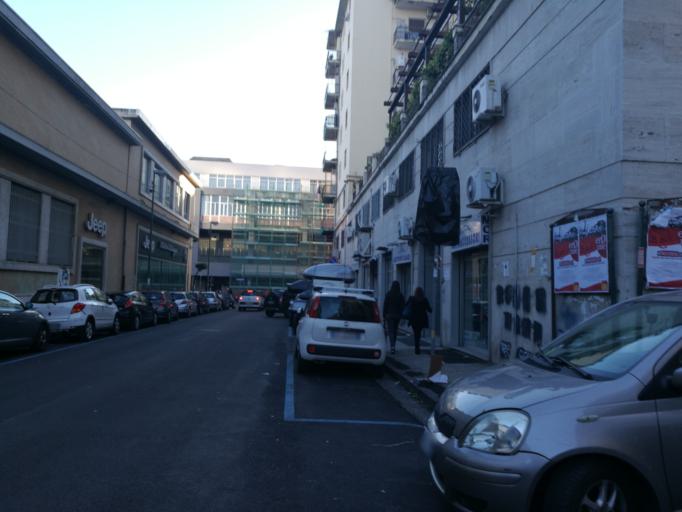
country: IT
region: Campania
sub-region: Provincia di Napoli
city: Napoli
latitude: 40.8553
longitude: 14.2760
